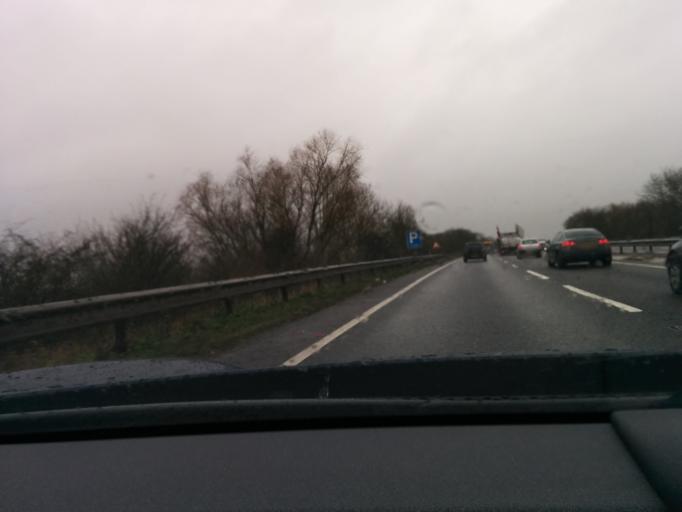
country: GB
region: England
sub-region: Oxfordshire
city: Abingdon
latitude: 51.6853
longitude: -1.2934
